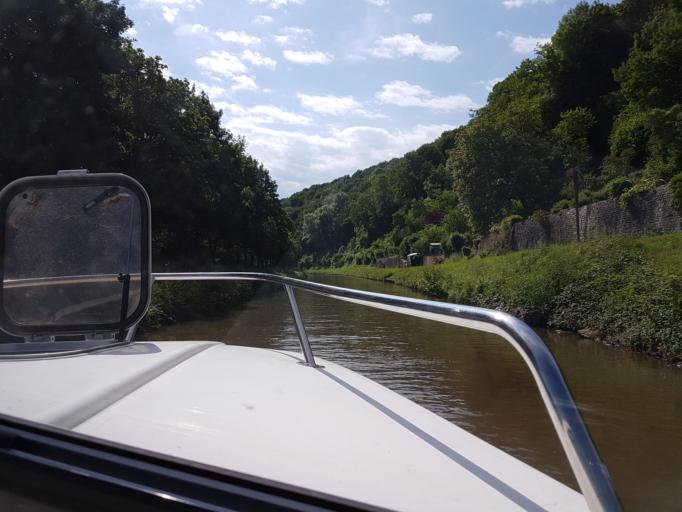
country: FR
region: Bourgogne
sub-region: Departement de la Nievre
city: Clamecy
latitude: 47.4516
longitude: 3.5281
